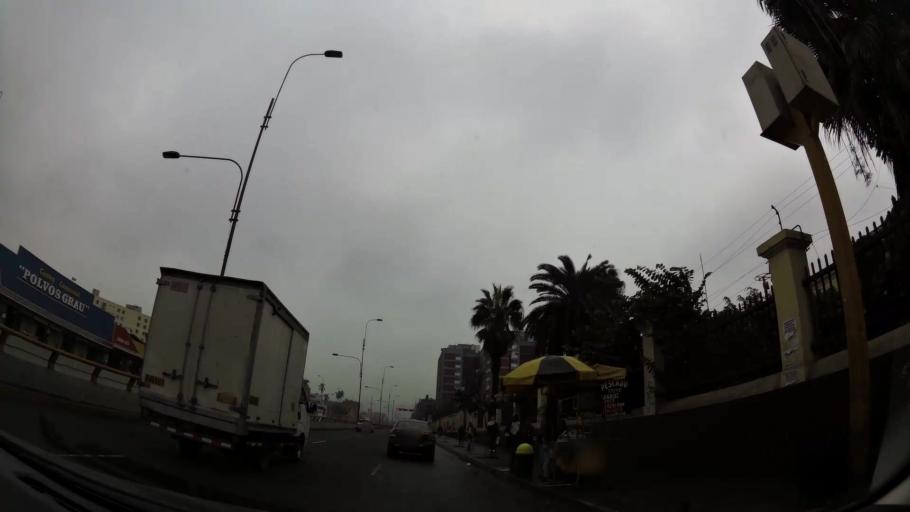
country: PE
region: Lima
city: Lima
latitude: -12.0593
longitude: -77.0265
